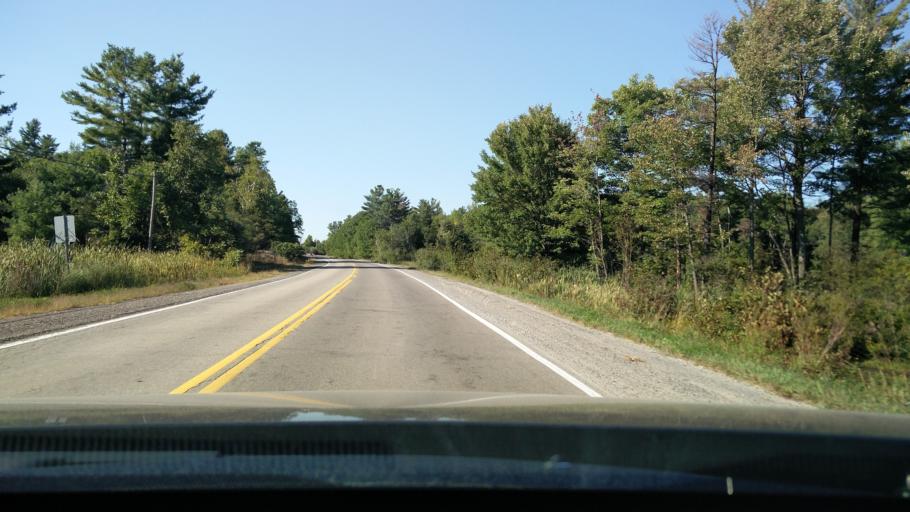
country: CA
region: Ontario
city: Perth
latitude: 44.6893
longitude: -76.3988
